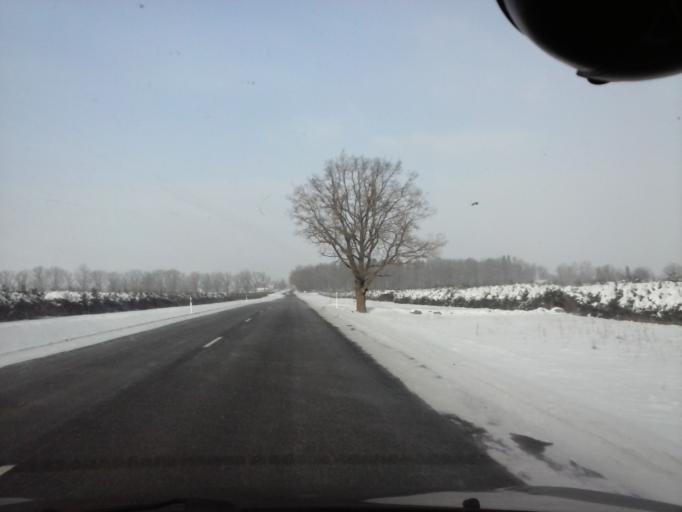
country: EE
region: Viljandimaa
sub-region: Abja vald
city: Abja-Paluoja
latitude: 58.3117
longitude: 25.3007
